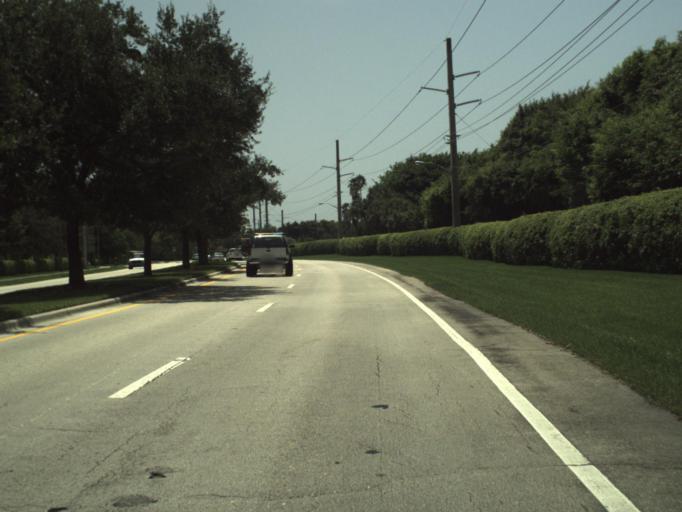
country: US
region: Florida
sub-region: Palm Beach County
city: Boca Del Mar
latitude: 26.3825
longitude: -80.1473
